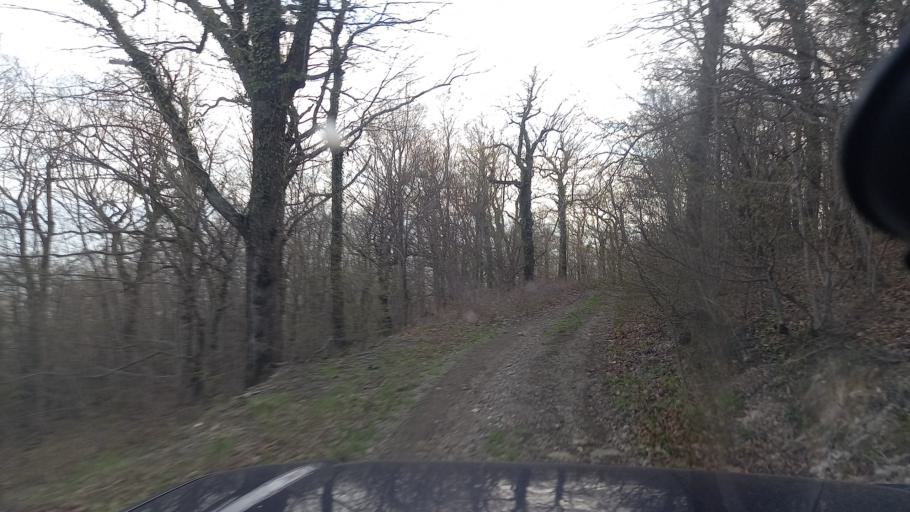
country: RU
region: Krasnodarskiy
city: Arkhipo-Osipovka
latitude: 44.3573
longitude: 38.5524
